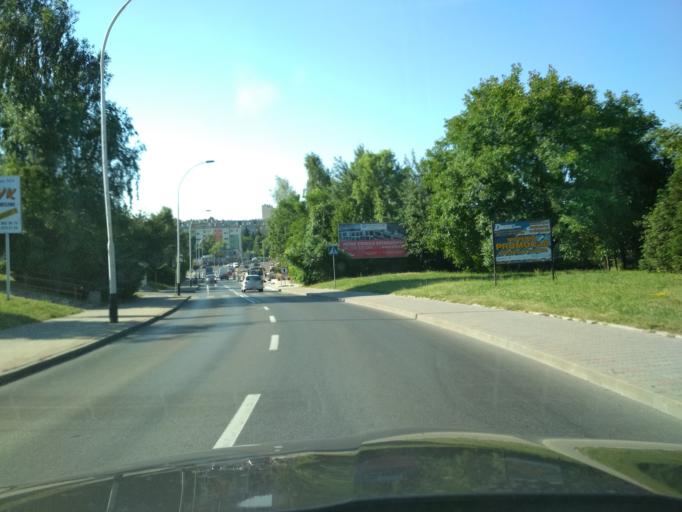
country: PL
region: Subcarpathian Voivodeship
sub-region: Rzeszow
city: Rzeszow
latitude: 50.0578
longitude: 21.9772
